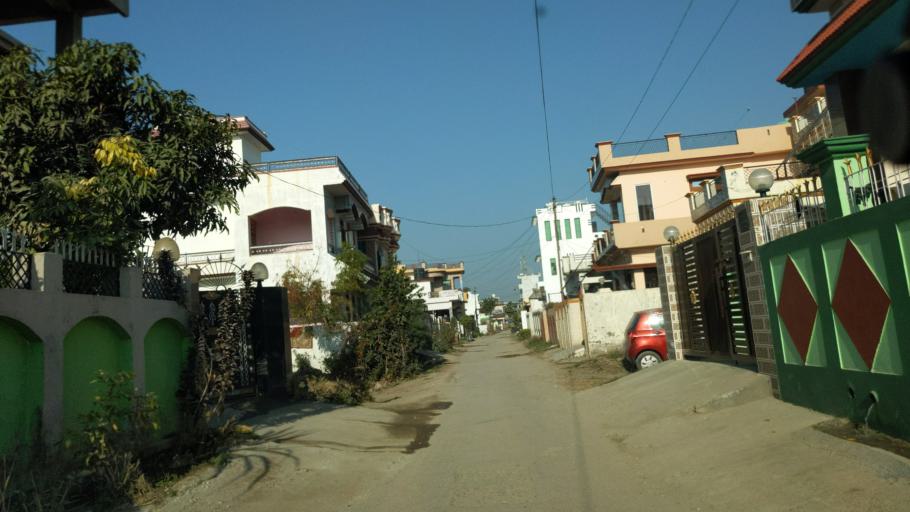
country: IN
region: Uttarakhand
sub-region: Naini Tal
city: Haldwani
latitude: 29.2068
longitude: 79.4969
